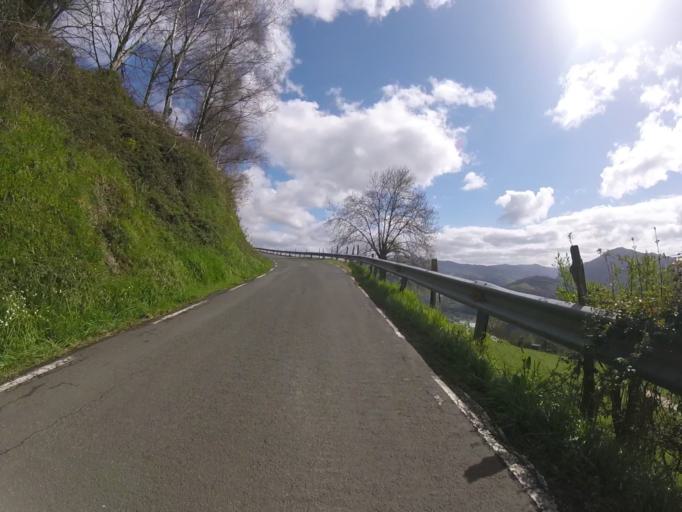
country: ES
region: Basque Country
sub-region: Provincia de Guipuzcoa
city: Tolosa
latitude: 43.1299
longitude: -2.1006
